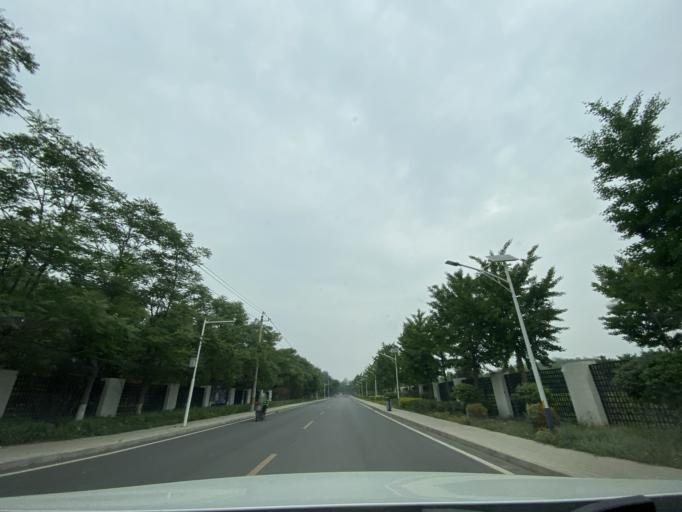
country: CN
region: Beijing
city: Sijiqing
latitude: 39.9363
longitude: 116.2392
